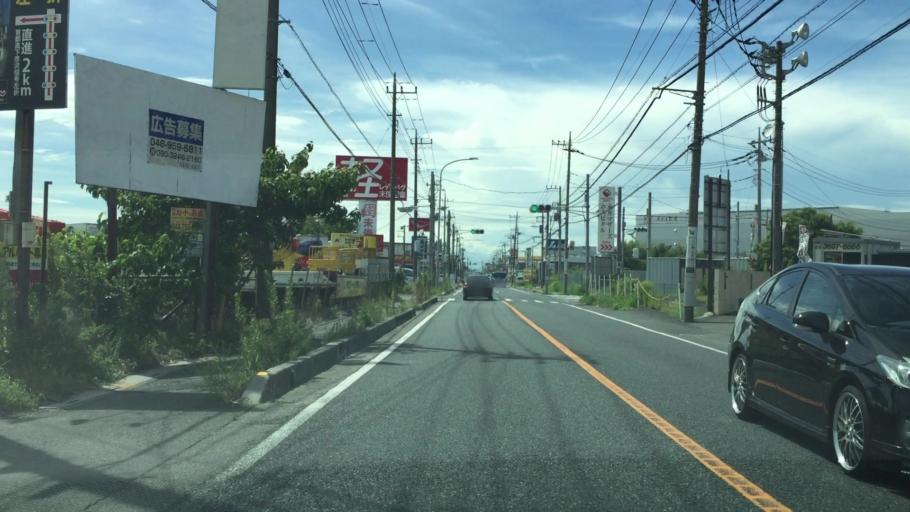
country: JP
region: Chiba
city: Nagareyama
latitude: 35.8483
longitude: 139.8672
